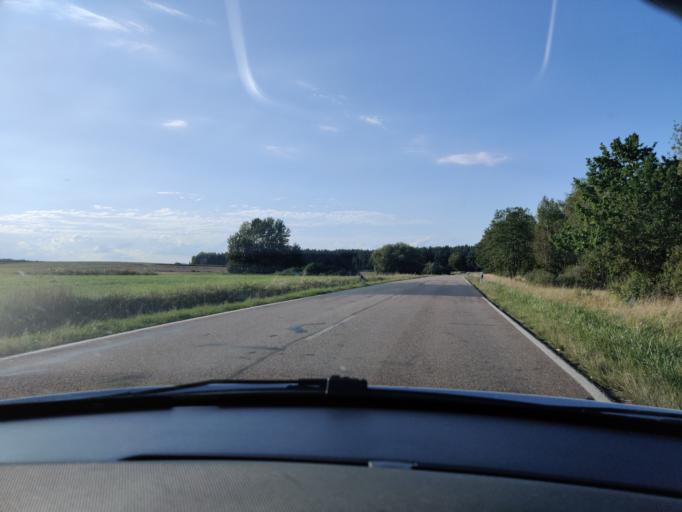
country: DE
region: Bavaria
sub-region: Upper Palatinate
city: Schwarzenfeld
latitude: 49.4018
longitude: 12.1312
